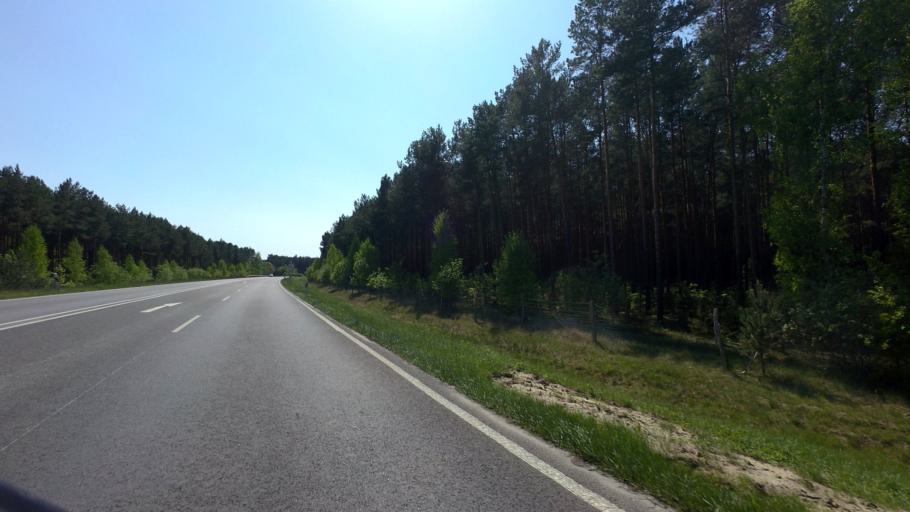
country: DE
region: Brandenburg
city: Beeskow
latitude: 52.1527
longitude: 14.2157
